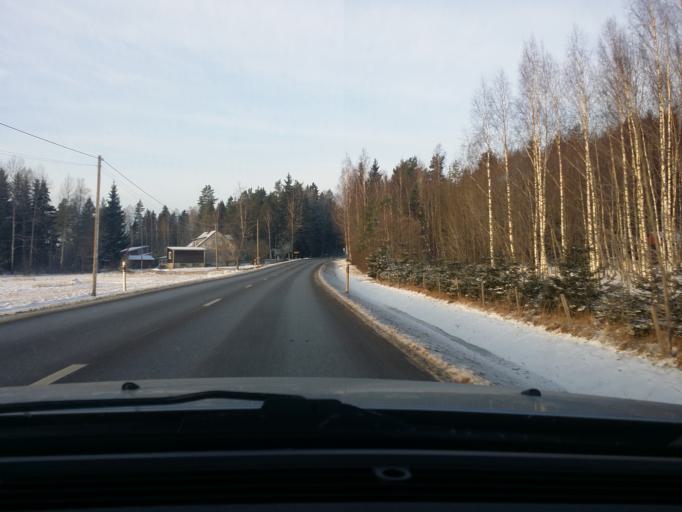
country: SE
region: OErebro
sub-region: Lindesbergs Kommun
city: Frovi
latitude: 59.5082
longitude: 15.3607
